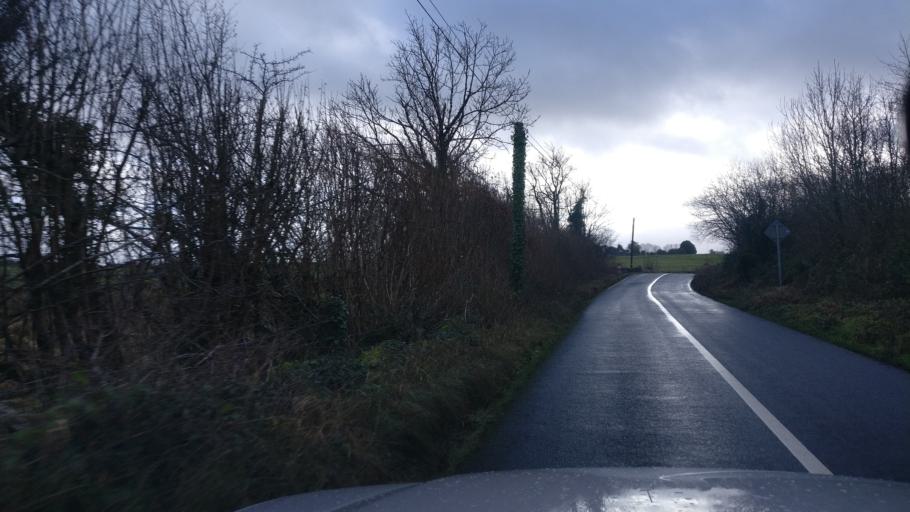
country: IE
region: Connaught
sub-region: County Galway
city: Loughrea
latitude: 53.2408
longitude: -8.6209
